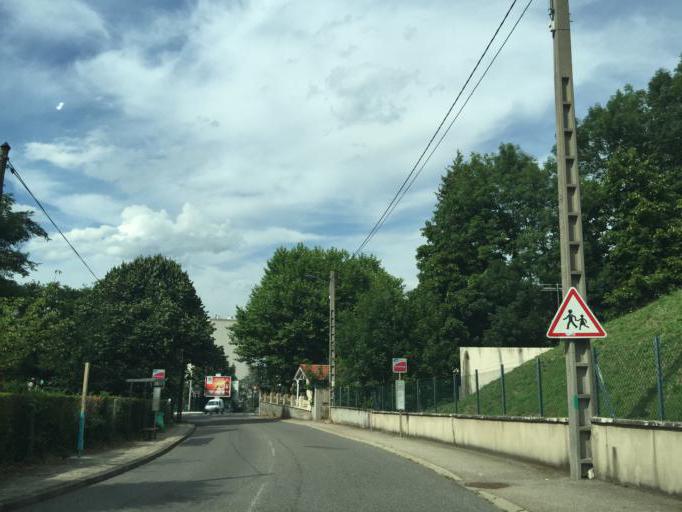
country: FR
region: Rhone-Alpes
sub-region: Departement de la Loire
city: Saint-Etienne
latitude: 45.4155
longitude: 4.4107
